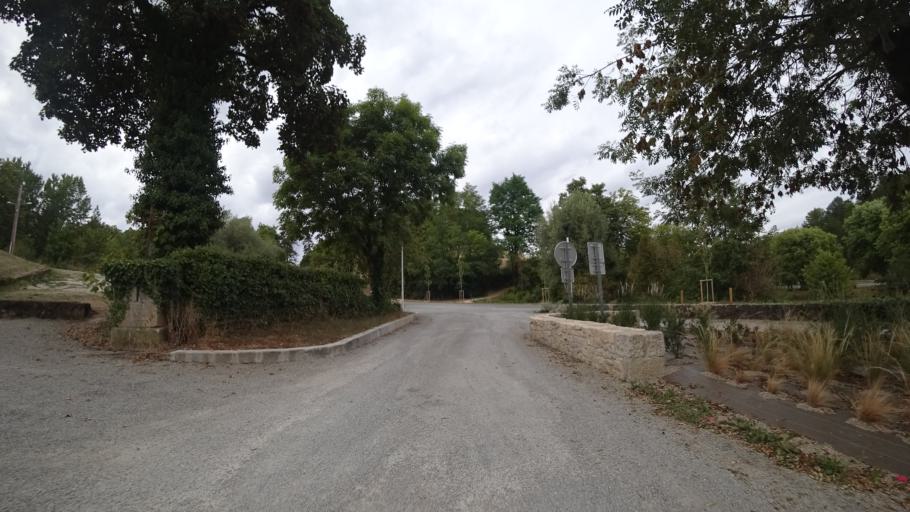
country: FR
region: Midi-Pyrenees
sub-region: Departement de l'Aveyron
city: Rodez
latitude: 44.3781
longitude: 2.5648
